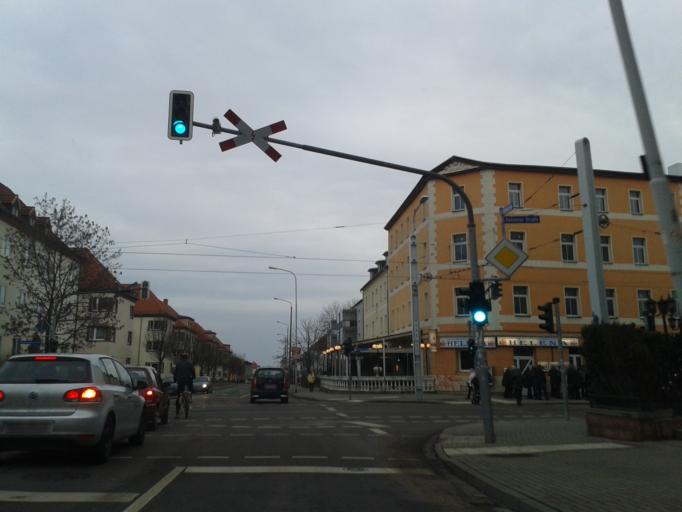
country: DE
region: Saxony-Anhalt
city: Halle (Saale)
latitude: 51.4630
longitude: 11.9713
